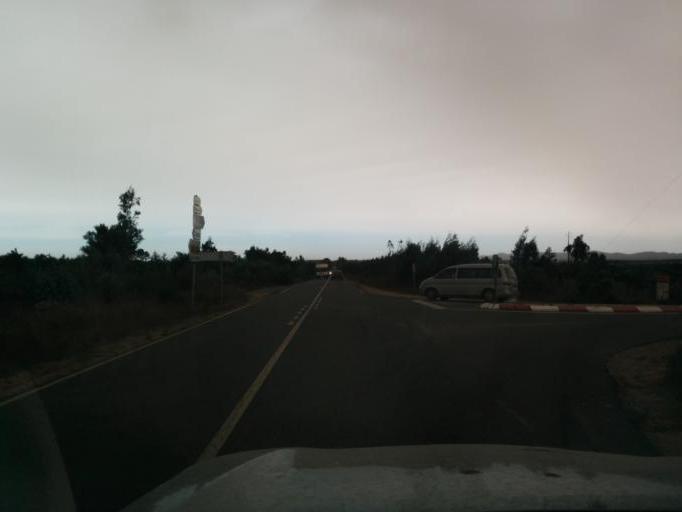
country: PT
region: Beja
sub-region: Odemira
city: Sao Teotonio
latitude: 37.5724
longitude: -8.7373
